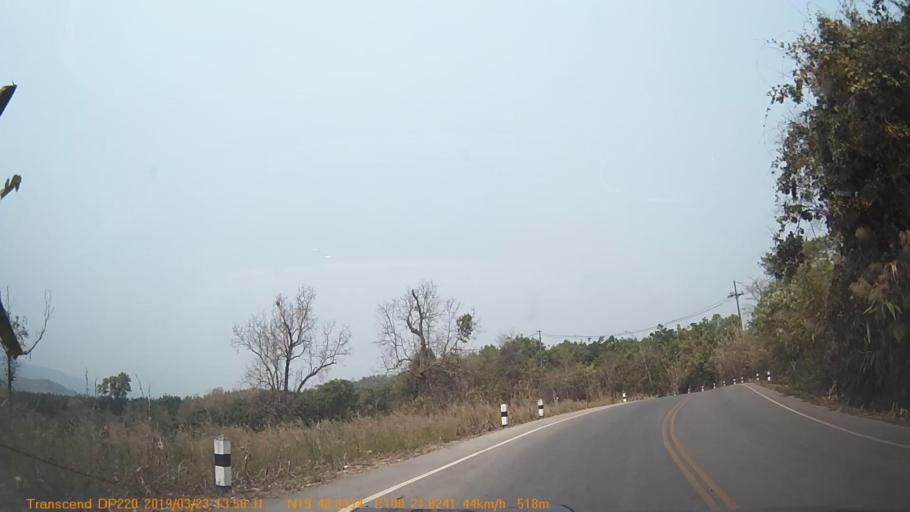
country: TH
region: Chiang Rai
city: Khun Tan
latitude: 19.8140
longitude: 100.3638
